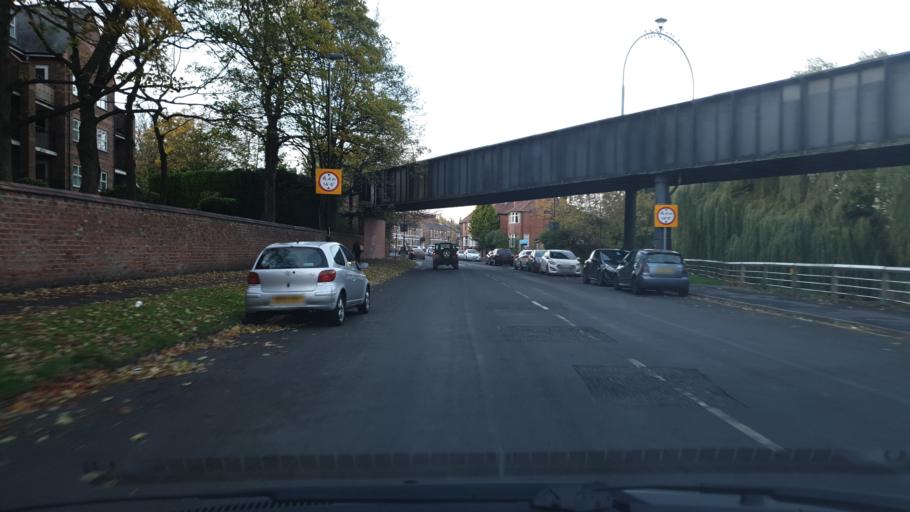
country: GB
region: England
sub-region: City of York
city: York
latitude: 53.9708
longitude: -1.0736
